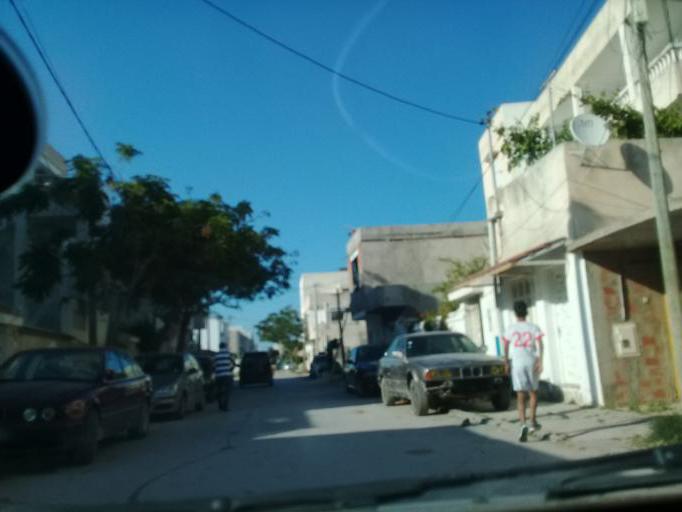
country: TN
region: Tunis
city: La Goulette
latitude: 36.8206
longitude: 10.3058
